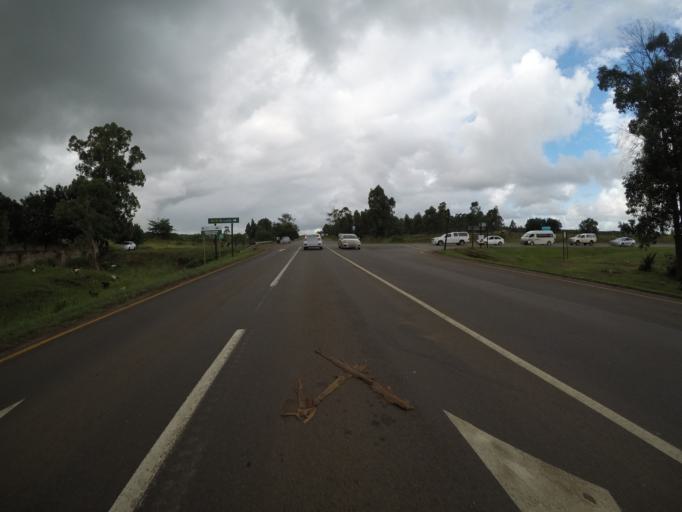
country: ZA
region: KwaZulu-Natal
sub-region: uMkhanyakude District Municipality
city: Mtubatuba
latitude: -28.4100
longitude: 32.1842
